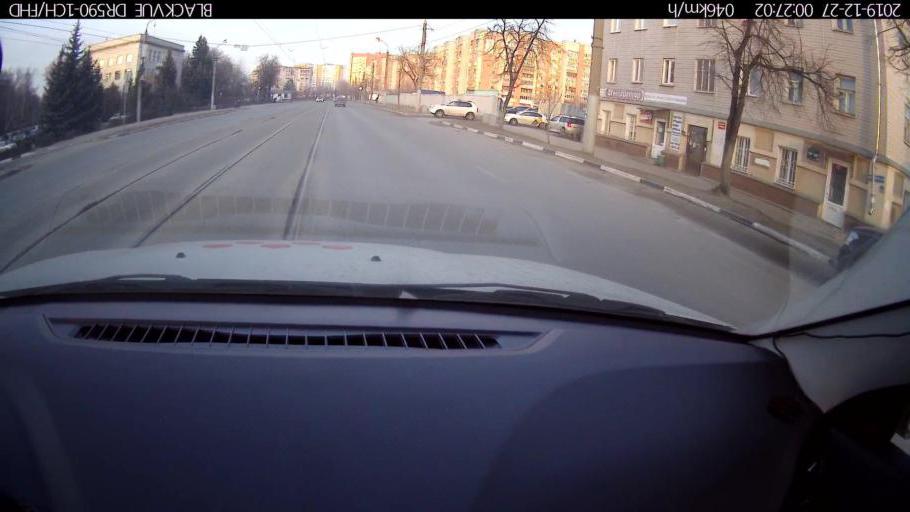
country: RU
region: Nizjnij Novgorod
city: Nizhniy Novgorod
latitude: 56.3103
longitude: 43.9354
